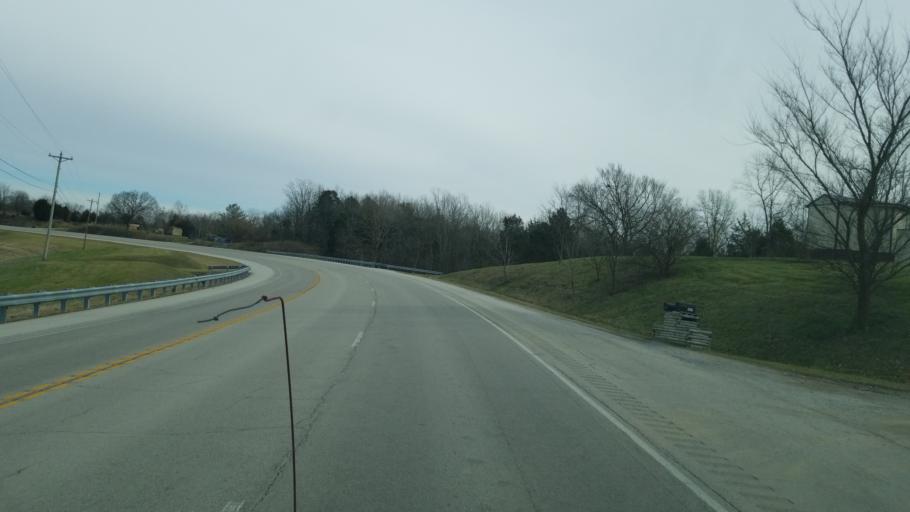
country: US
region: Kentucky
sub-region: Robertson County
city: Mount Olivet
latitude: 38.4469
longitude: -83.9708
